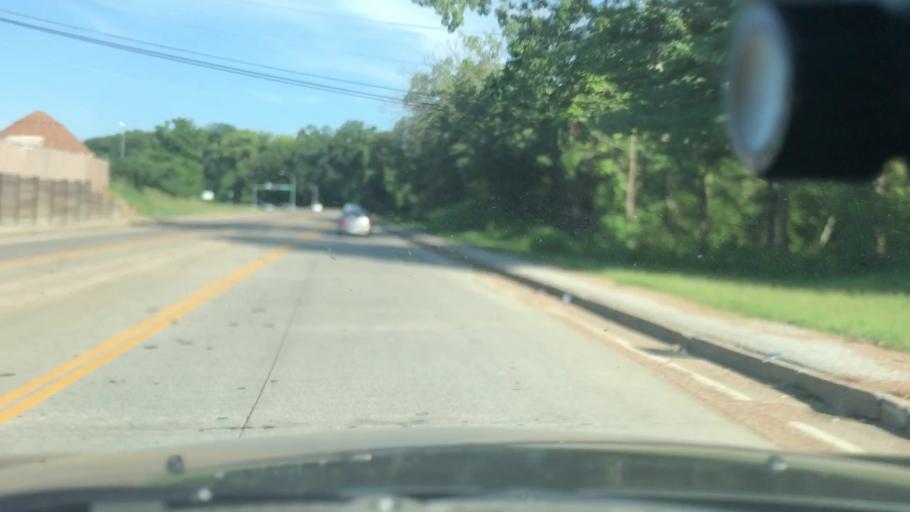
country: US
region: Missouri
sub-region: Saint Louis County
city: Frontenac
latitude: 38.6397
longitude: -90.4386
